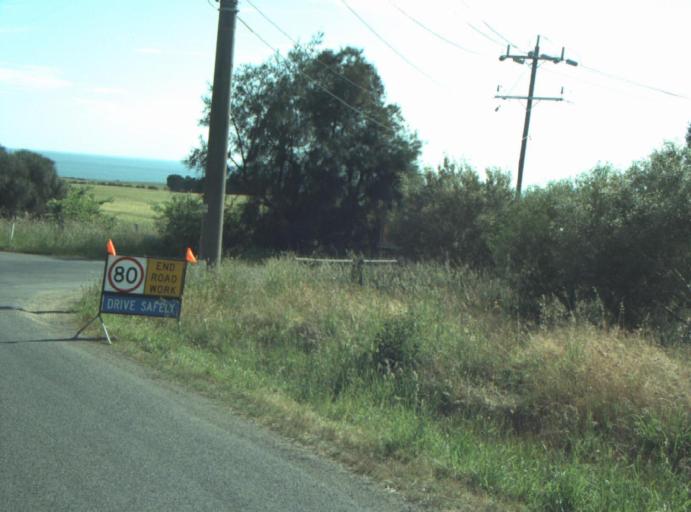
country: AU
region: Victoria
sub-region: Greater Geelong
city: Clifton Springs
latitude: -38.1704
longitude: 144.5150
